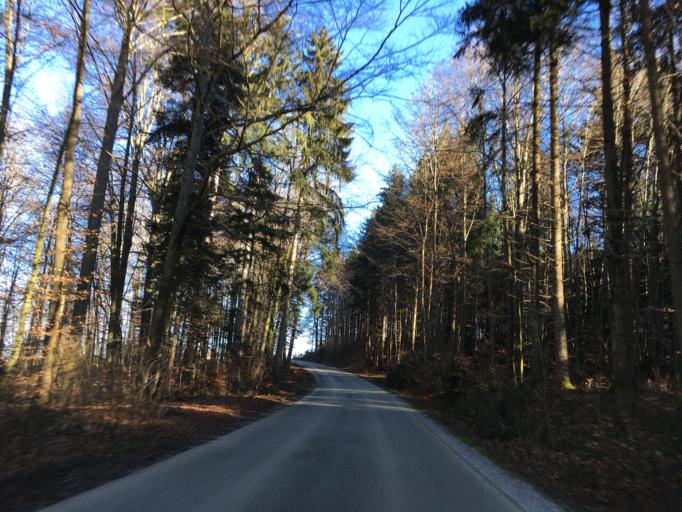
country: DE
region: Bavaria
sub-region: Upper Bavaria
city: Amerang
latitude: 48.0264
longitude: 12.3356
